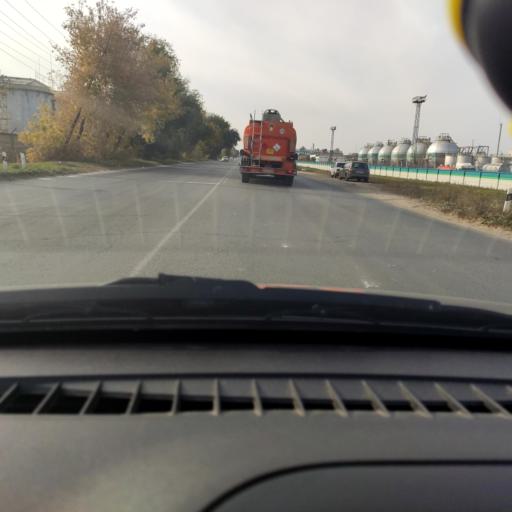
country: RU
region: Samara
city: Tol'yatti
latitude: 53.5316
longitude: 49.4592
